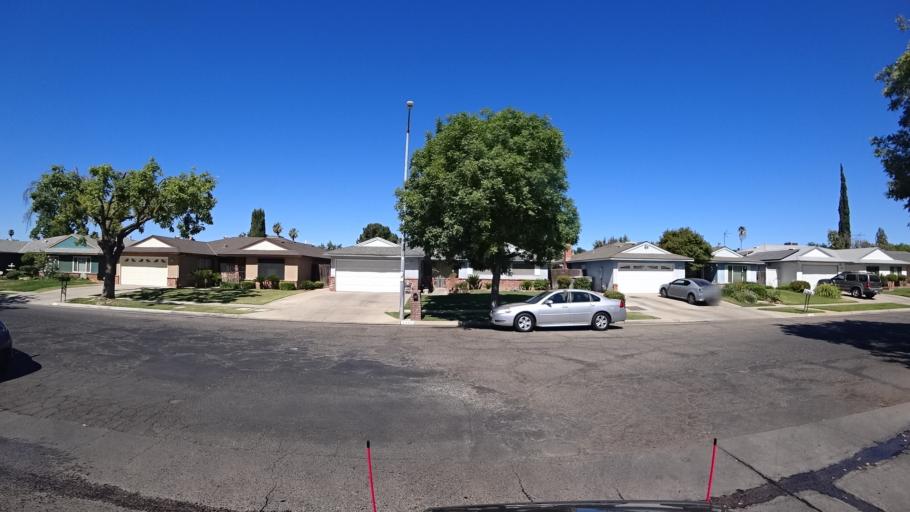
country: US
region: California
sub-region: Fresno County
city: West Park
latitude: 36.8009
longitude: -119.8492
